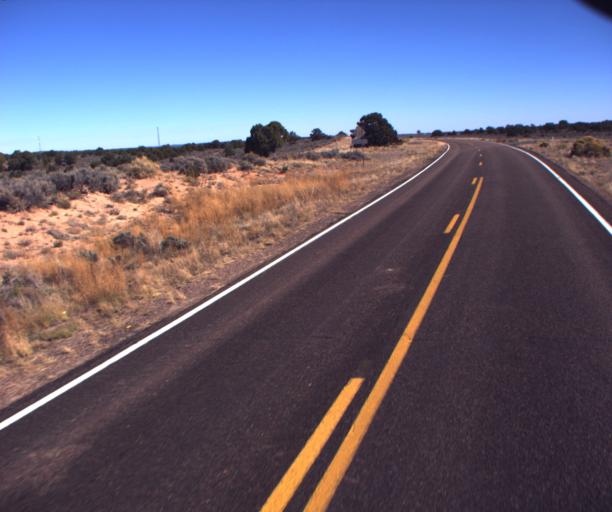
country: US
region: Arizona
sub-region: Navajo County
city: First Mesa
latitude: 35.7332
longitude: -110.1000
